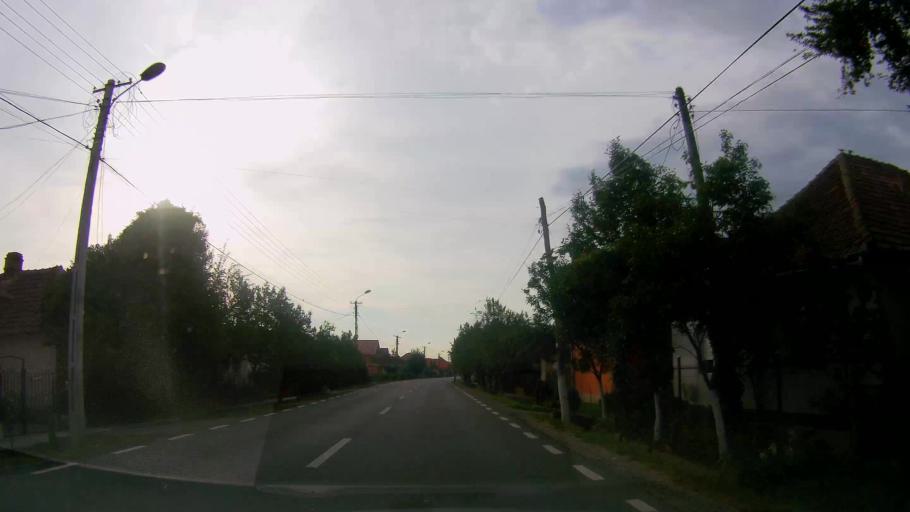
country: RO
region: Satu Mare
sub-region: Comuna Turulung
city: Turulung
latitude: 47.9462
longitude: 23.0732
